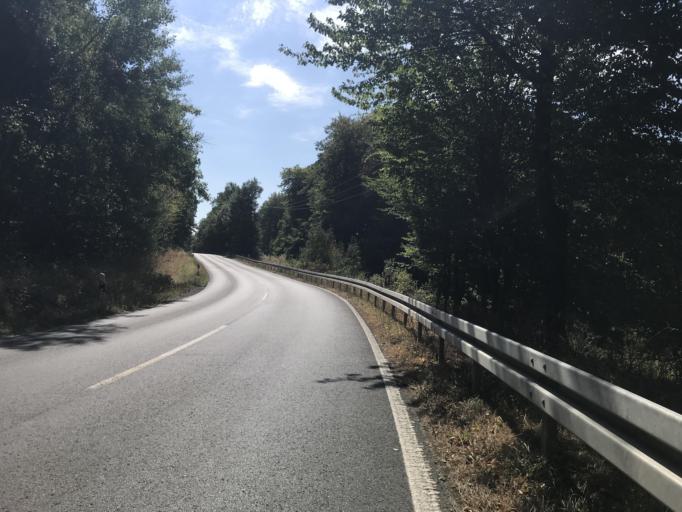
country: DE
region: Hesse
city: Geisenheim
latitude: 50.0290
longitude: 7.9519
